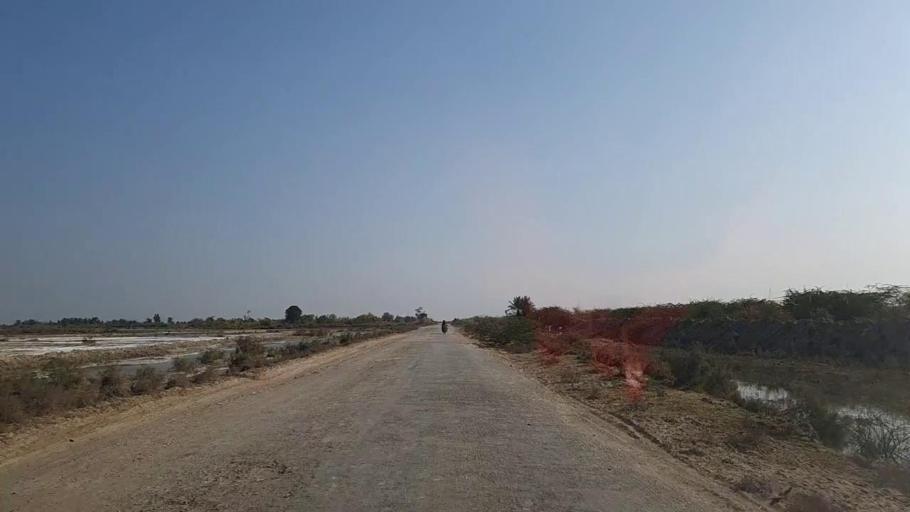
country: PK
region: Sindh
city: Tando Mittha Khan
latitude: 25.9244
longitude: 69.0675
